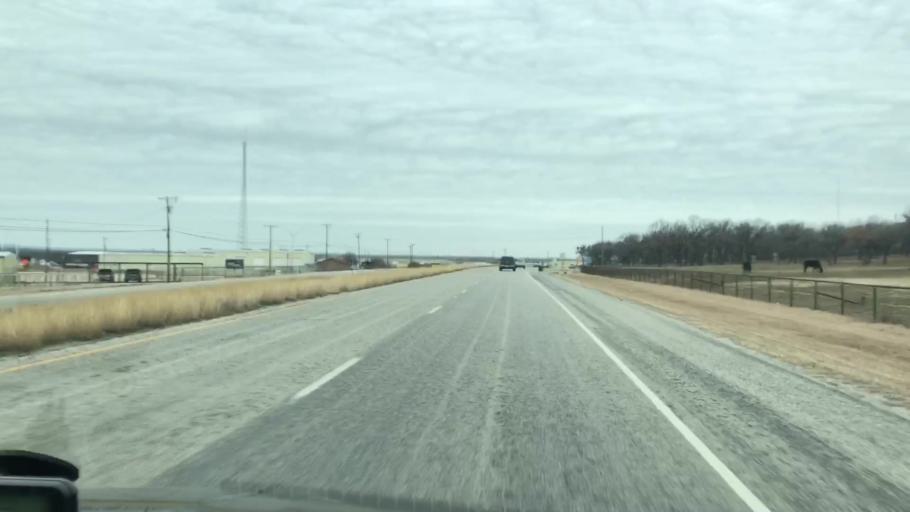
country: US
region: Texas
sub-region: Jack County
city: Jacksboro
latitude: 33.1941
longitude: -98.1425
